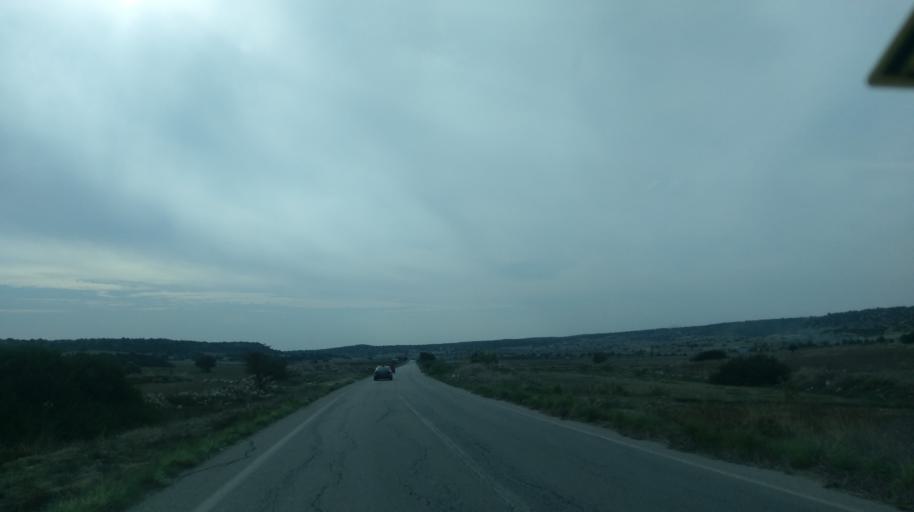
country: CY
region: Ammochostos
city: Leonarisso
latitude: 35.4633
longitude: 34.1380
